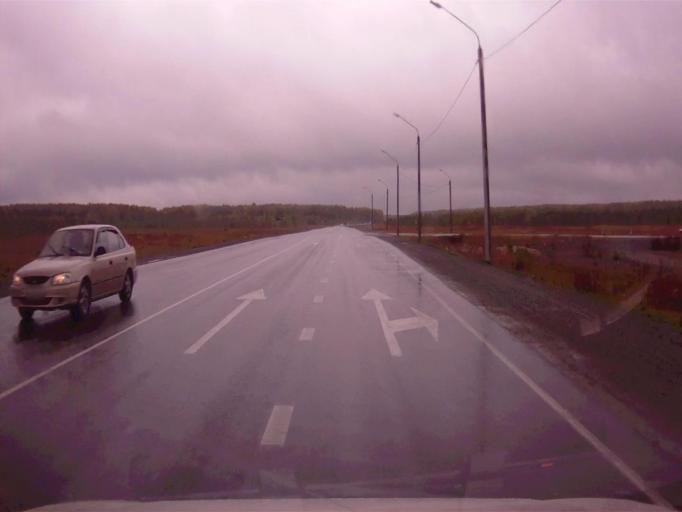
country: RU
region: Chelyabinsk
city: Tayginka
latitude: 55.5016
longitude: 60.6365
